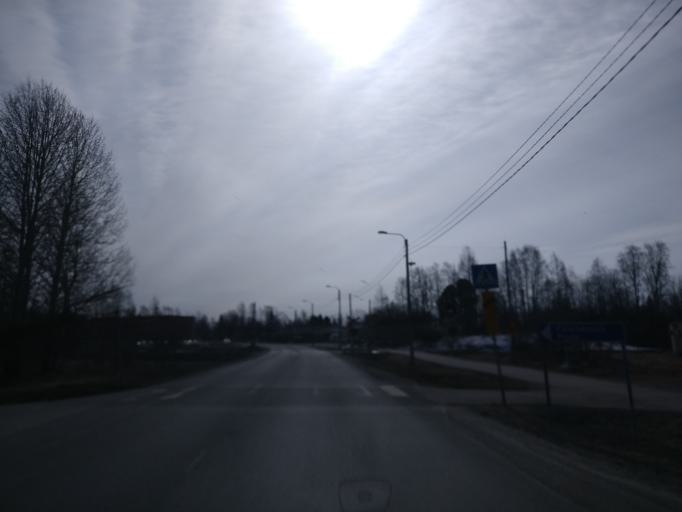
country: FI
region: Lapland
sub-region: Kemi-Tornio
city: Kemi
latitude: 65.7525
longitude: 24.5539
